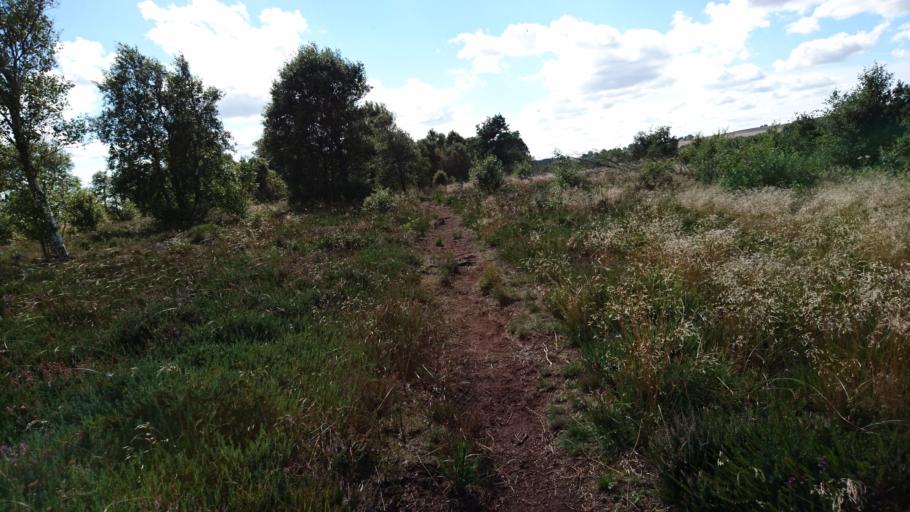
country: DK
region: North Denmark
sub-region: Alborg Kommune
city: Storvorde
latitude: 56.8669
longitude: 10.1732
